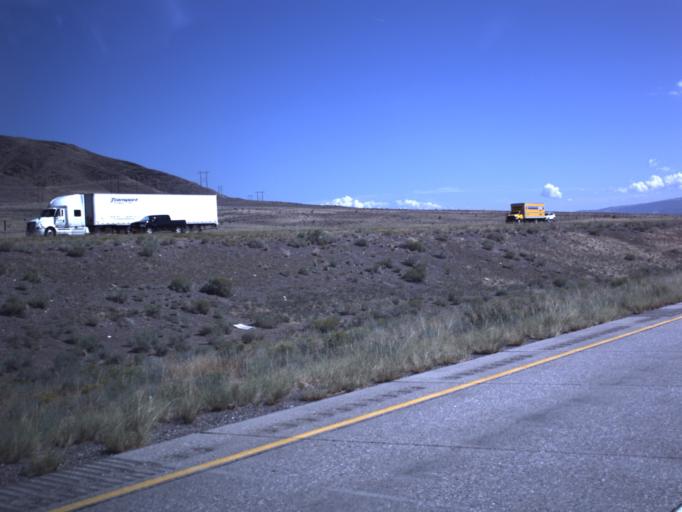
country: US
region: Utah
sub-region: Sevier County
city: Monroe
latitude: 38.6583
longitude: -112.1923
